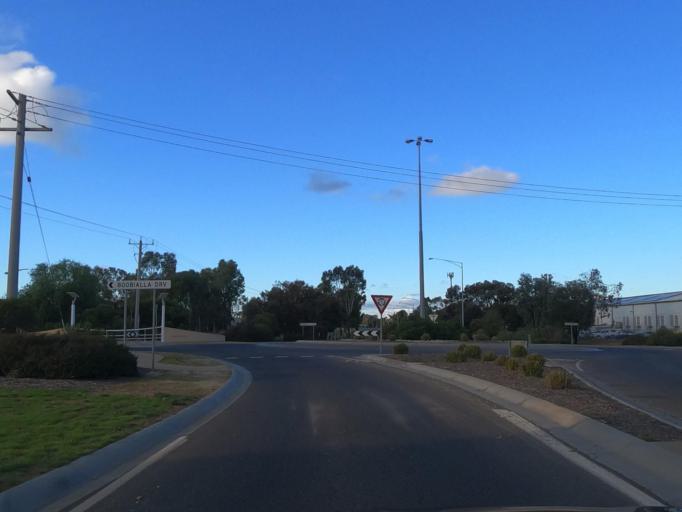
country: AU
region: Victoria
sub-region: Swan Hill
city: Swan Hill
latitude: -35.3432
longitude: 143.5310
